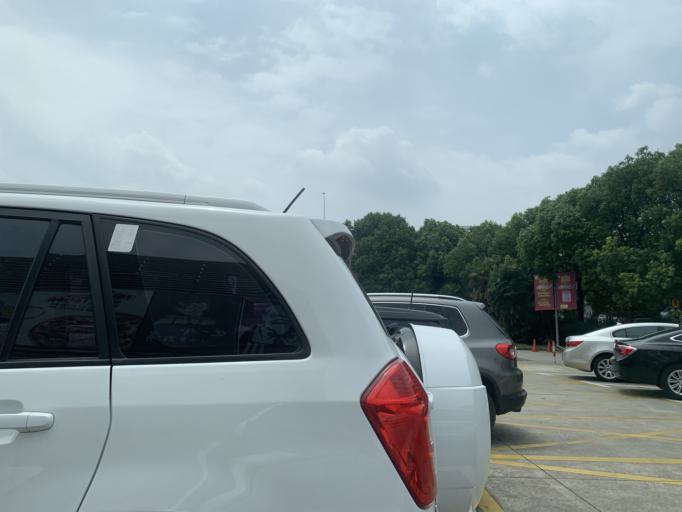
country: CN
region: Shanghai Shi
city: Huamu
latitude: 31.2069
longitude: 121.5548
